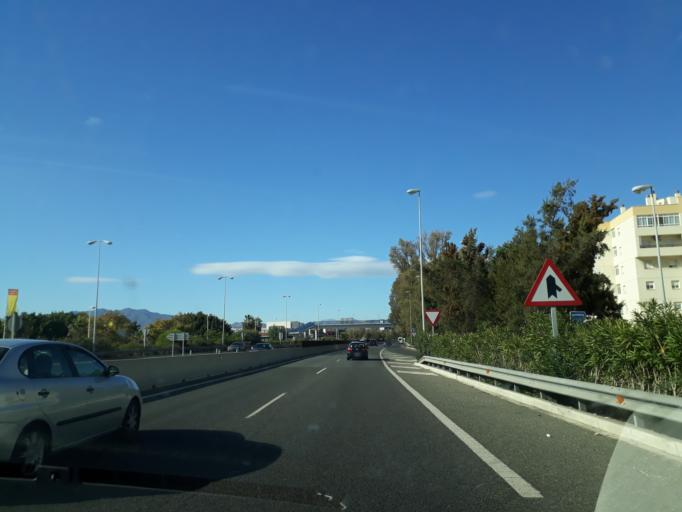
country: ES
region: Andalusia
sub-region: Provincia de Malaga
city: Fuengirola
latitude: 36.5323
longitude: -4.6305
